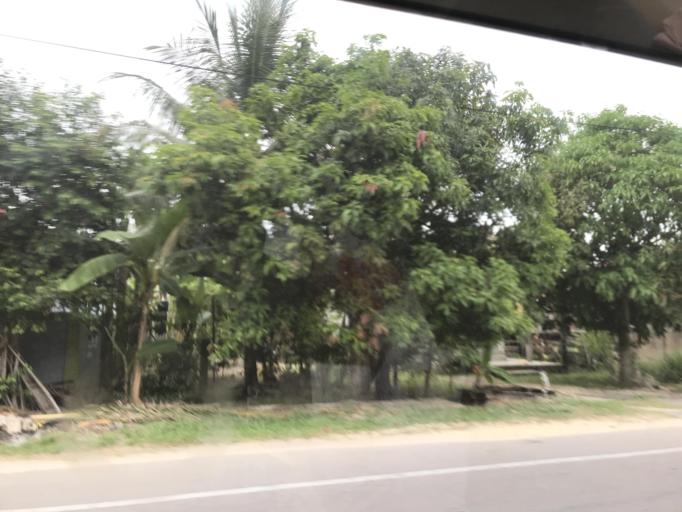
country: MY
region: Kelantan
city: Kota Bharu
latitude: 6.1429
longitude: 102.2184
